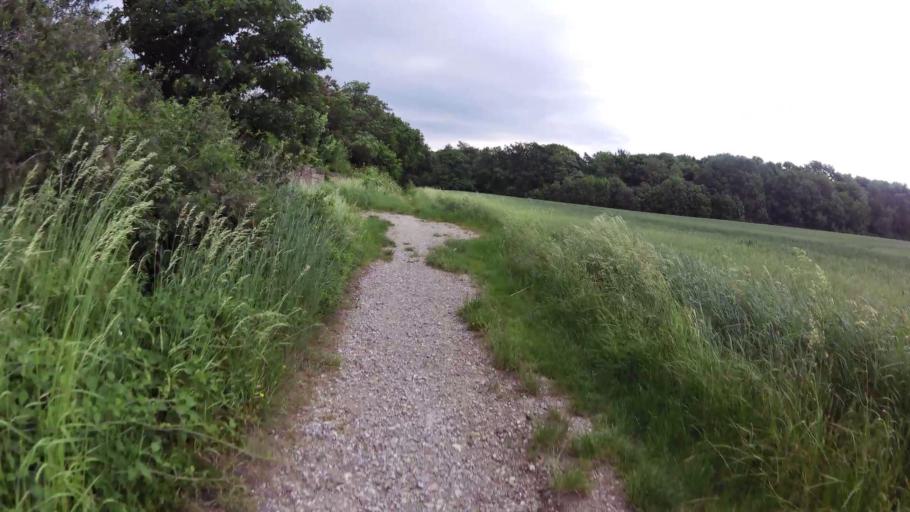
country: DE
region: Thuringia
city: Weimar
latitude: 50.9660
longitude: 11.3186
